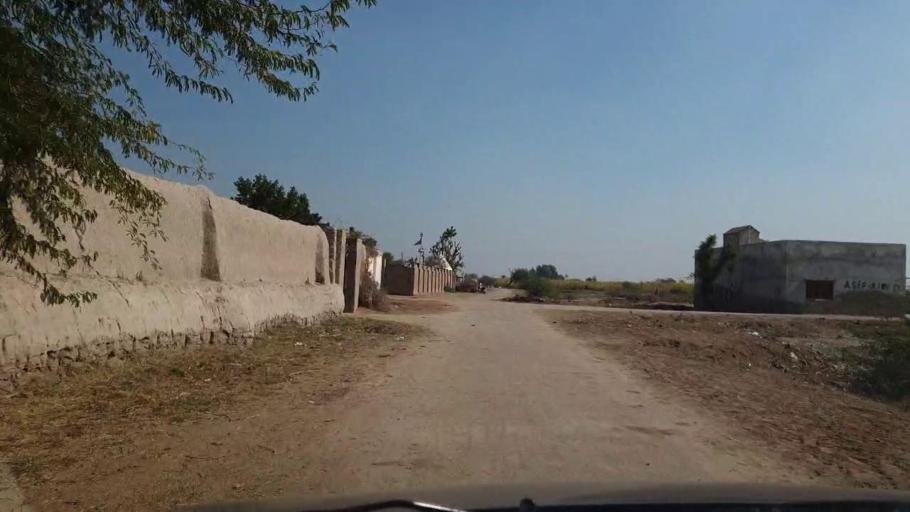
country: PK
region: Sindh
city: Jhol
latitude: 25.9088
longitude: 68.8072
